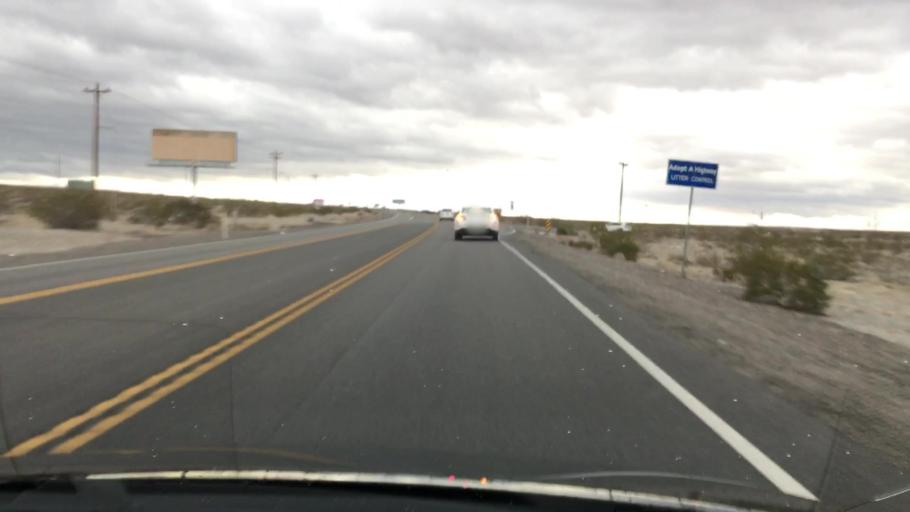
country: US
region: Nevada
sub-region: Nye County
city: Pahrump
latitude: 36.1510
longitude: -115.8950
